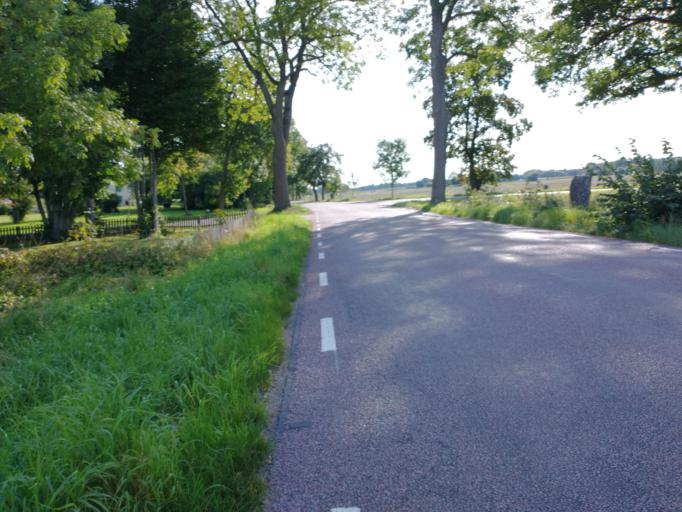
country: SE
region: Kalmar
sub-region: Kalmar Kommun
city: Lindsdal
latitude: 56.7857
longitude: 16.3245
